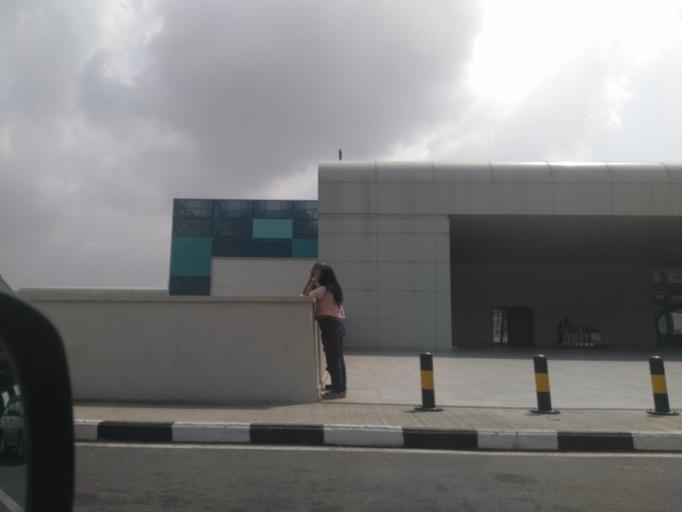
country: GH
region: Greater Accra
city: Accra
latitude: 5.6027
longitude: -0.1732
